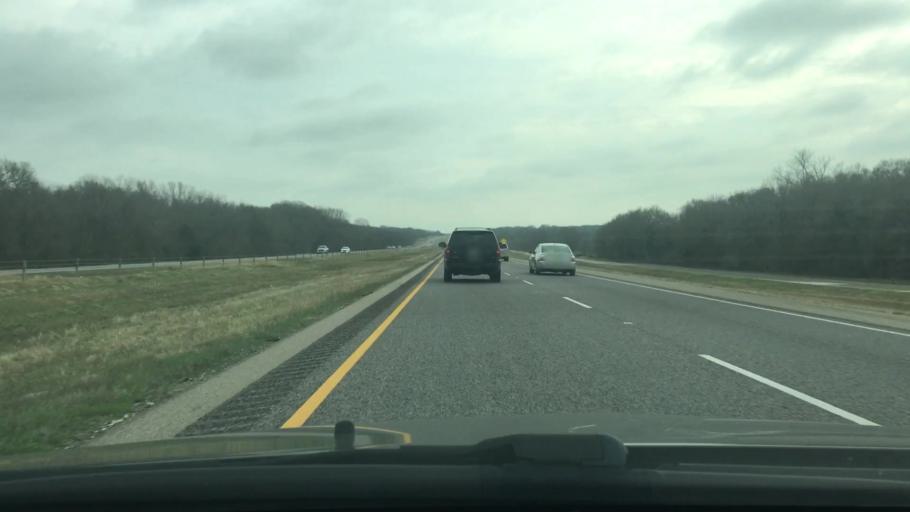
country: US
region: Texas
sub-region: Freestone County
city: Fairfield
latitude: 31.6554
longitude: -96.1610
